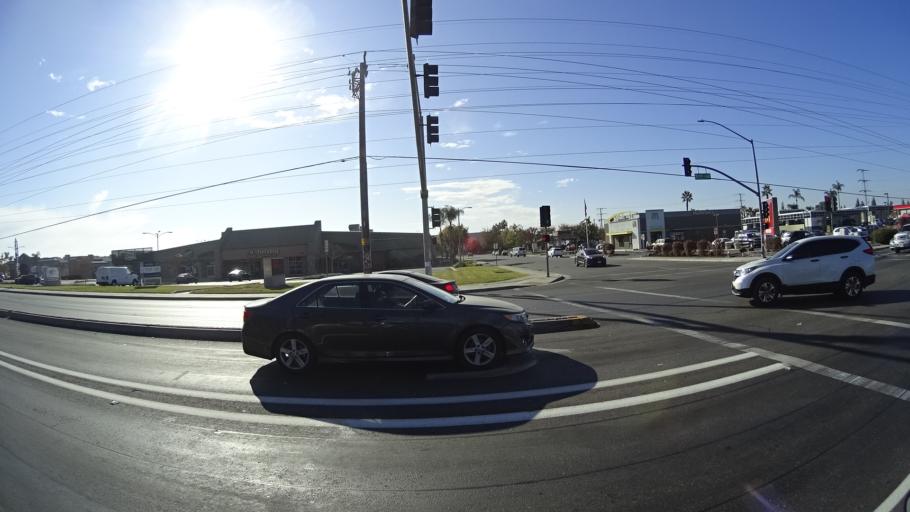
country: US
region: California
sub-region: Kern County
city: Greenacres
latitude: 35.3183
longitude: -119.0894
